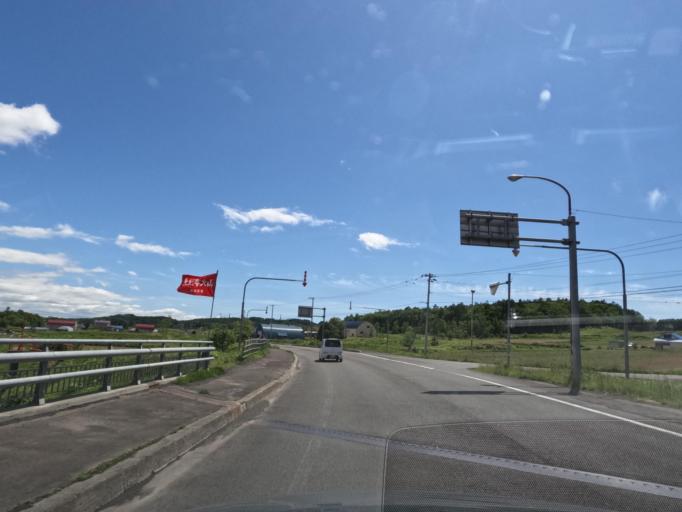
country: JP
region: Hokkaido
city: Iwamizawa
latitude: 43.1192
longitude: 141.8038
